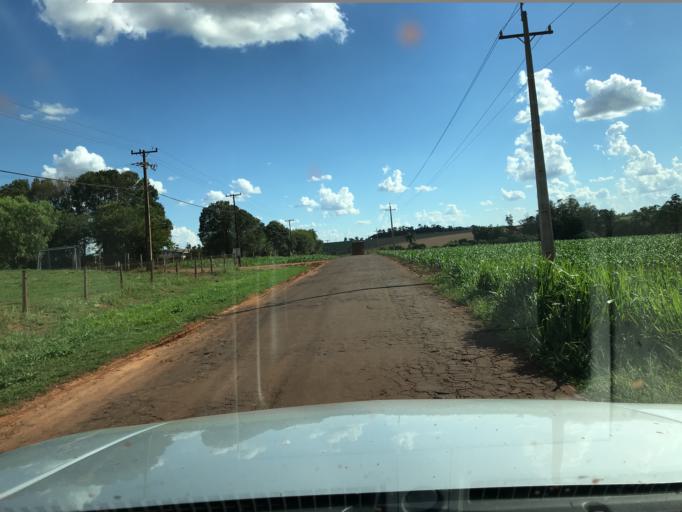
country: BR
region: Parana
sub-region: Palotina
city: Palotina
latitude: -24.2609
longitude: -53.8001
